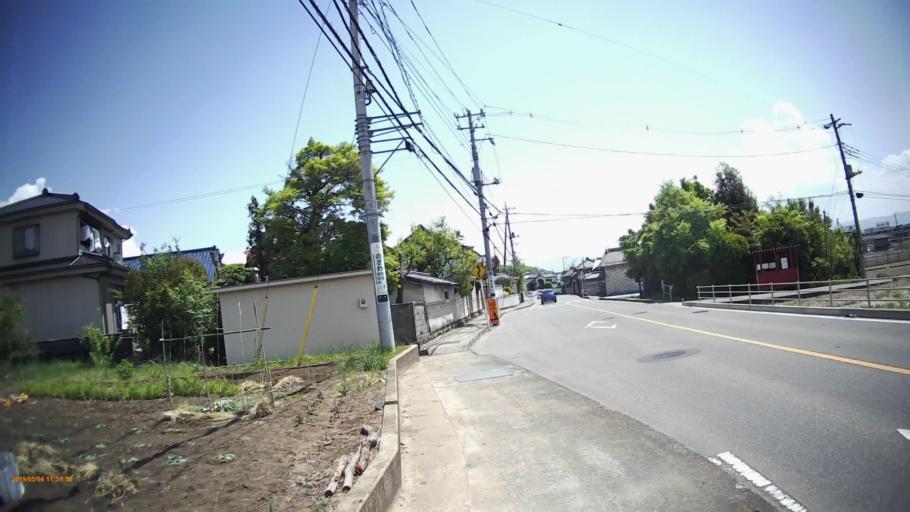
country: JP
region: Yamanashi
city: Nirasaki
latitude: 35.6895
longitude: 138.4816
